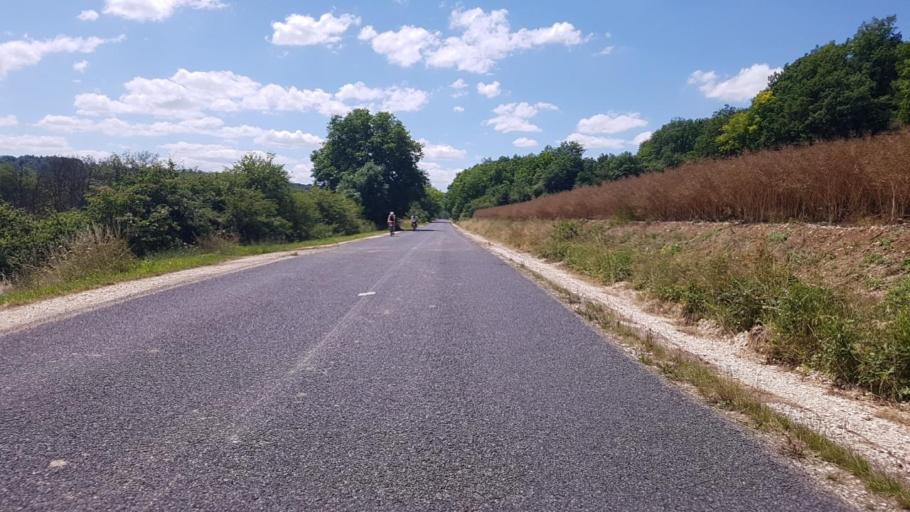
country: FR
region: Lorraine
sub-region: Departement de la Meuse
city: Ligny-en-Barrois
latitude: 48.6433
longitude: 5.3934
